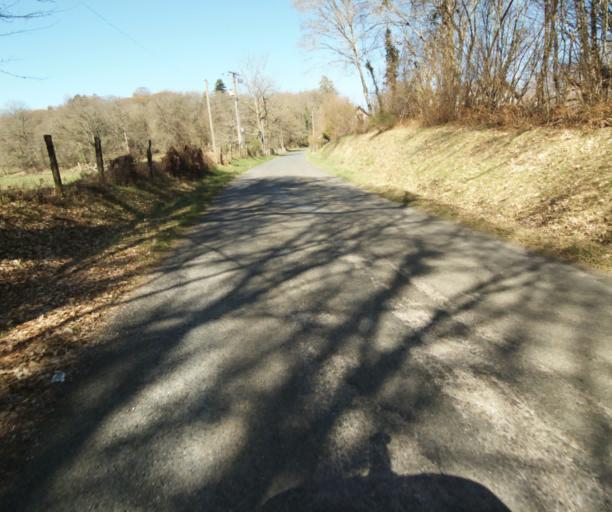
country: FR
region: Limousin
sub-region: Departement de la Correze
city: Saint-Clement
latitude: 45.3417
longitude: 1.6434
